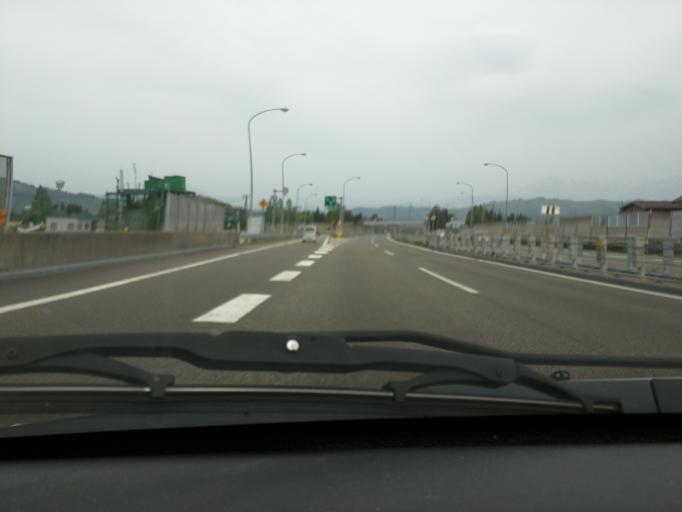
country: JP
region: Niigata
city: Ojiya
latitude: 37.2711
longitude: 138.8326
